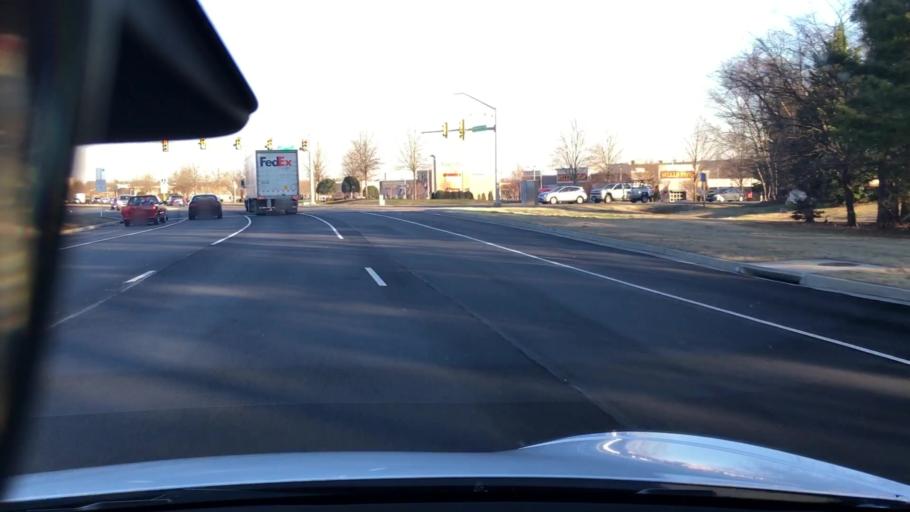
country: US
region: Virginia
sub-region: Henrico County
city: Montrose
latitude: 37.5233
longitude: -77.3524
